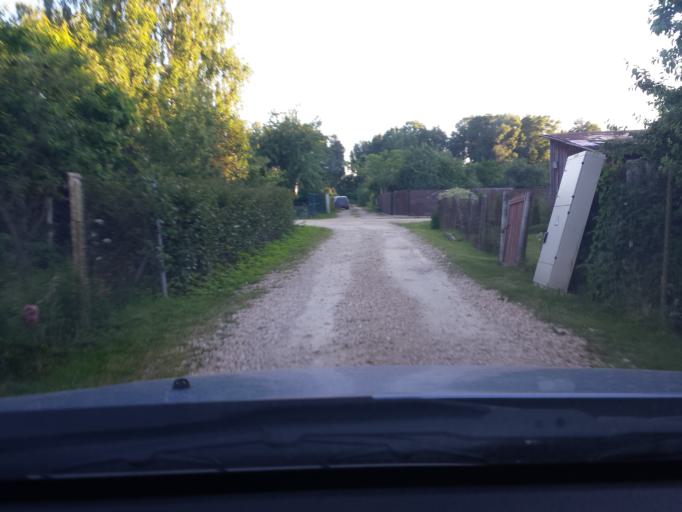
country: LV
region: Carnikava
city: Carnikava
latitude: 57.1246
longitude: 24.2355
